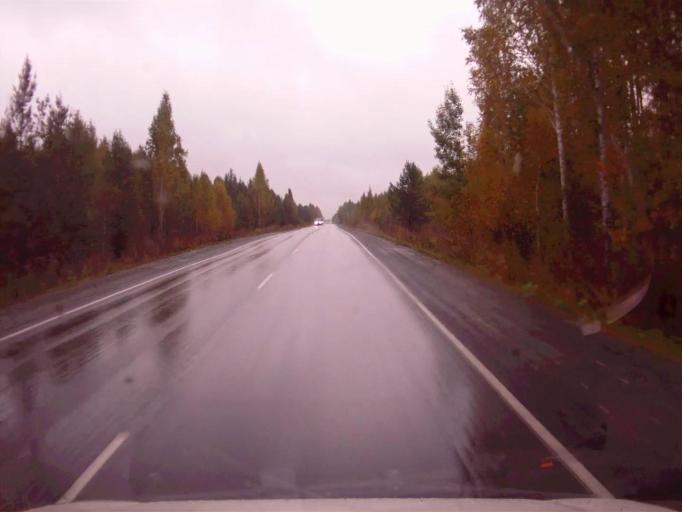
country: RU
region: Chelyabinsk
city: Tayginka
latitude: 55.5369
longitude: 60.6467
